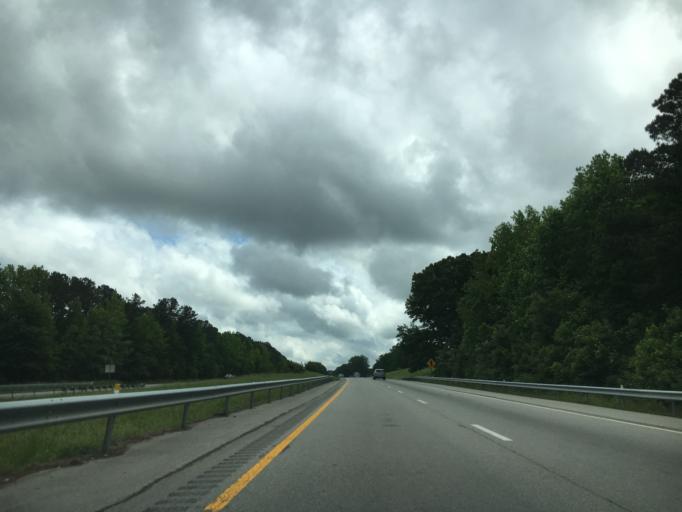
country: US
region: Virginia
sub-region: Mecklenburg County
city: South Hill
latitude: 36.7496
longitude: -78.0956
